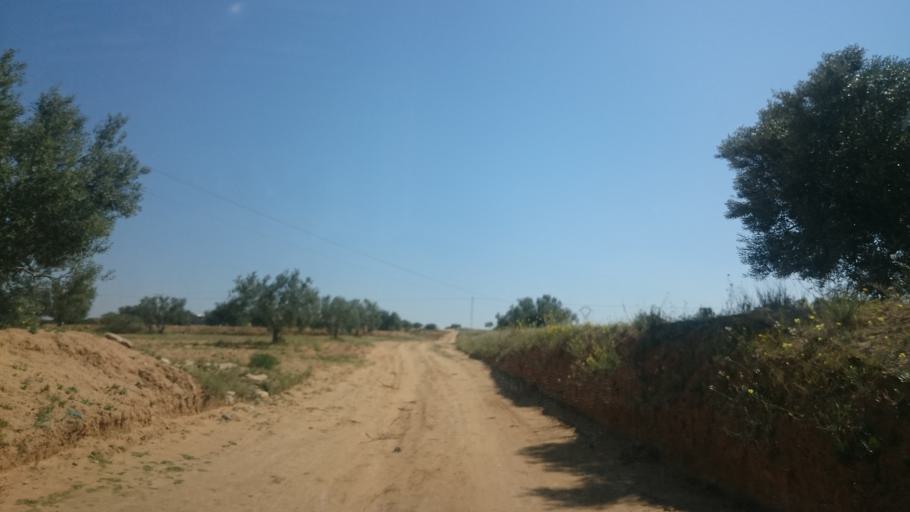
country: TN
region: Safaqis
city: Sfax
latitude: 34.7891
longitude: 10.5411
